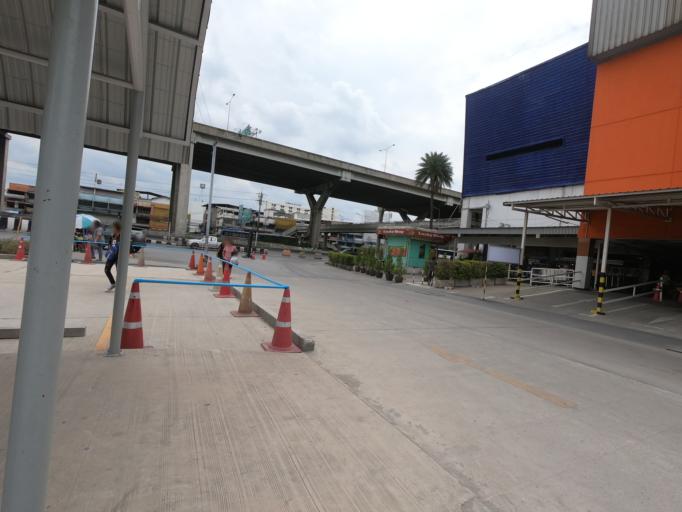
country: TH
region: Bangkok
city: Sai Mai
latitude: 13.9185
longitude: 100.6548
